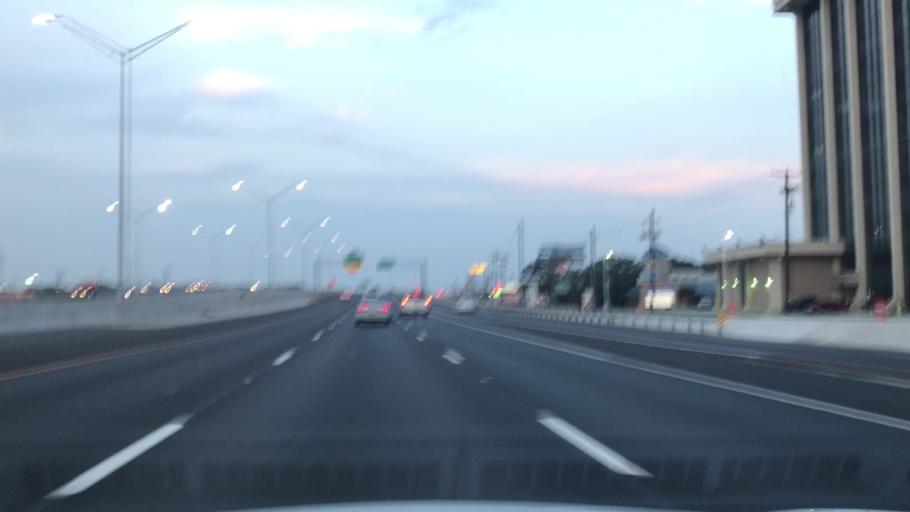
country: US
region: Texas
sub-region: Dallas County
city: Irving
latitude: 32.8364
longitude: -96.9553
